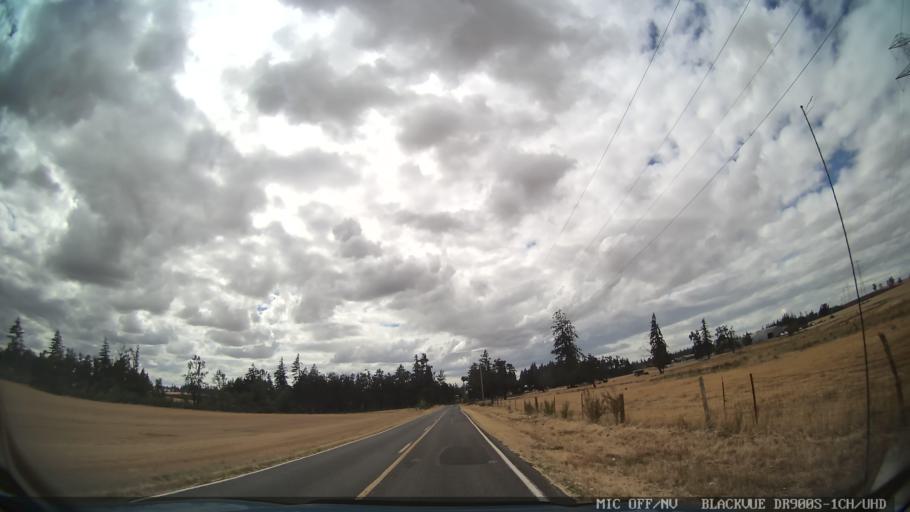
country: US
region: Oregon
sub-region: Marion County
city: Sublimity
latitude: 44.8443
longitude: -122.7699
